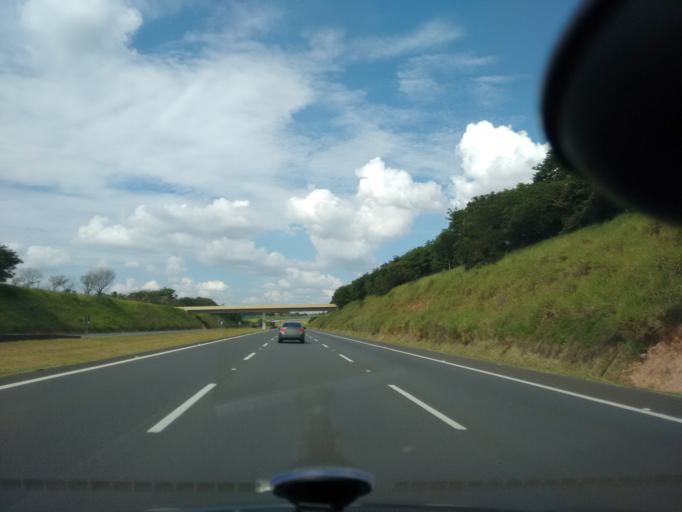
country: BR
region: Sao Paulo
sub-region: Sumare
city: Sumare
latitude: -22.8719
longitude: -47.2687
